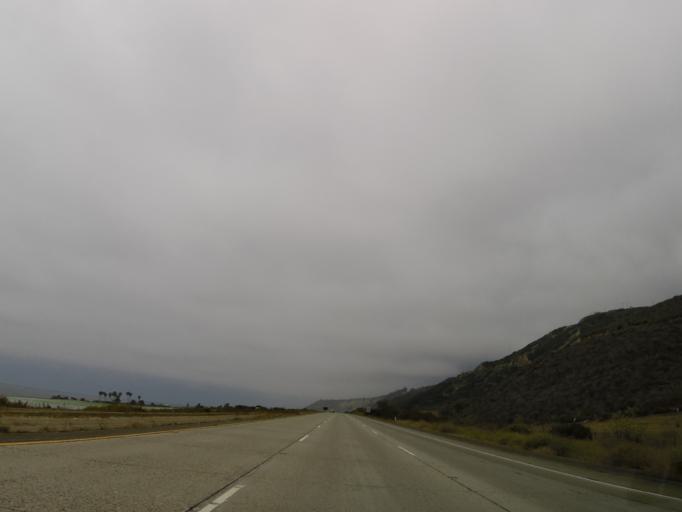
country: US
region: California
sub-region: Ventura County
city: Oak View
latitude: 34.3360
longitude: -119.4042
